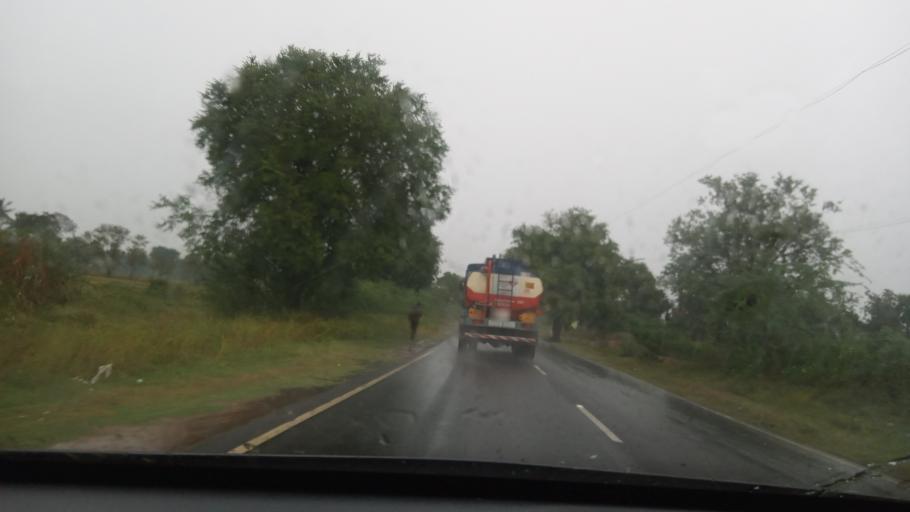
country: IN
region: Tamil Nadu
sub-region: Vellore
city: Kalavai
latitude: 12.8181
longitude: 79.4110
